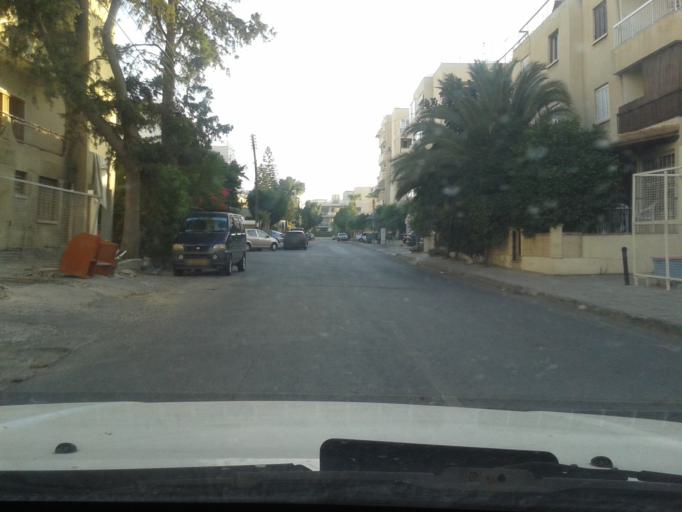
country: CY
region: Lefkosia
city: Nicosia
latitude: 35.1442
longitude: 33.3630
